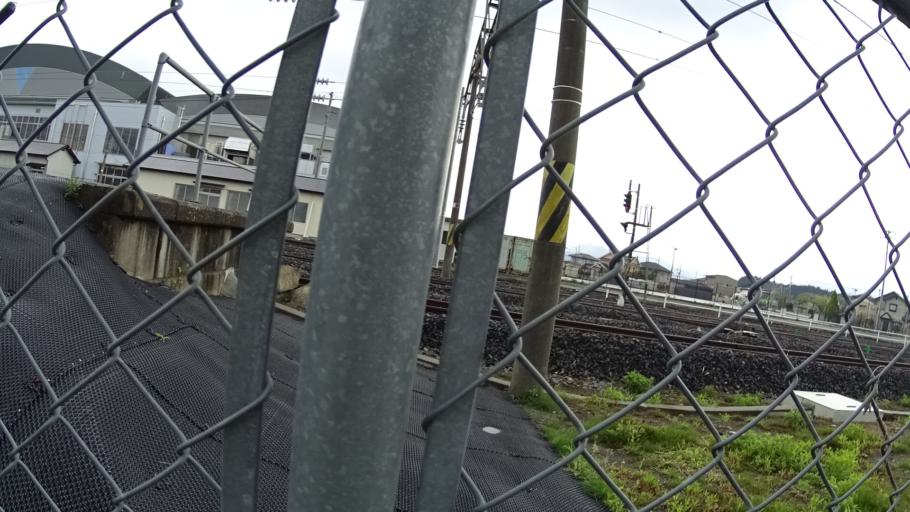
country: JP
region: Fukushima
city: Namie
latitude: 37.4930
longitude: 140.9884
